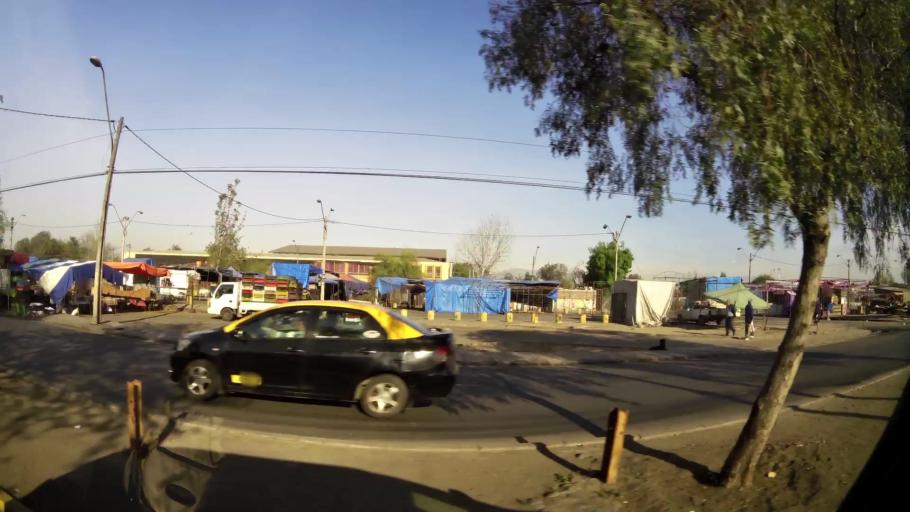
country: CL
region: Santiago Metropolitan
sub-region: Provincia de Santiago
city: Lo Prado
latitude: -33.4404
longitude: -70.7407
